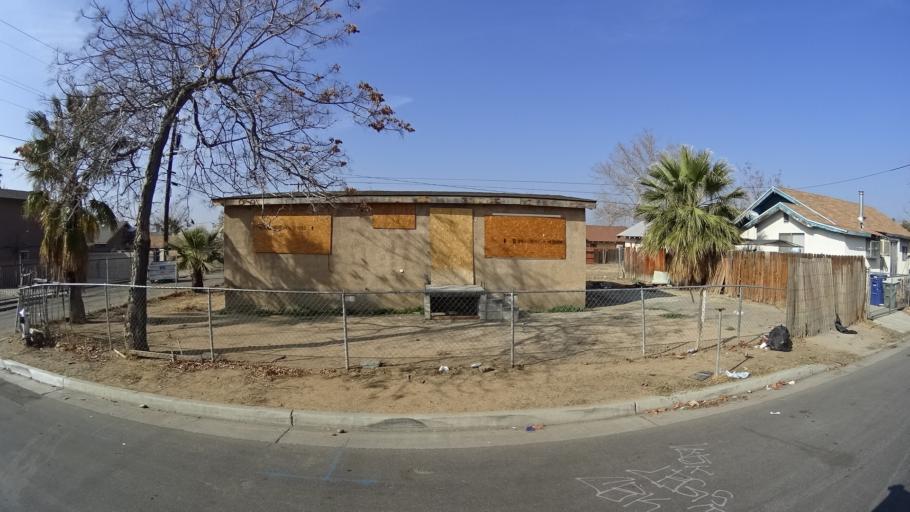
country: US
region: California
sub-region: Kern County
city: Bakersfield
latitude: 35.3805
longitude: -118.9815
